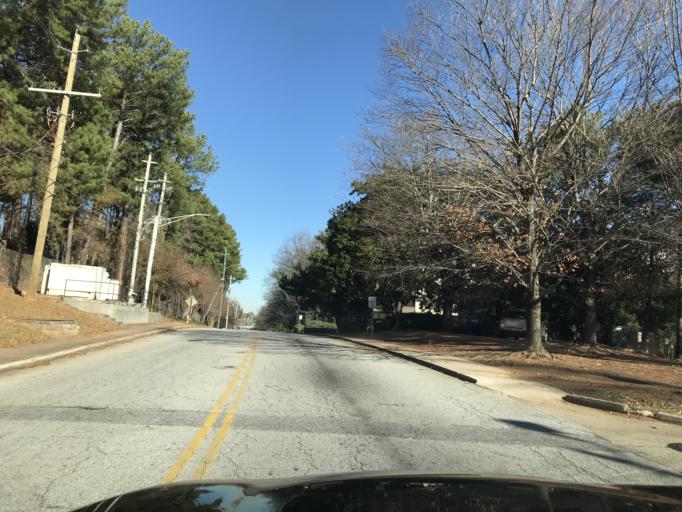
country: US
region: Georgia
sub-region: Fulton County
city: College Park
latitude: 33.6255
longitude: -84.4581
